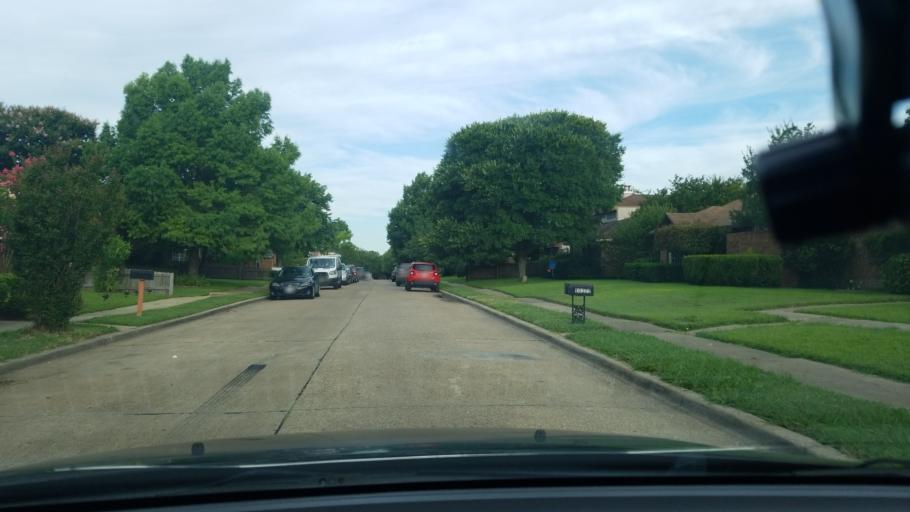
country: US
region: Texas
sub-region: Dallas County
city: Balch Springs
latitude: 32.7542
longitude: -96.6448
